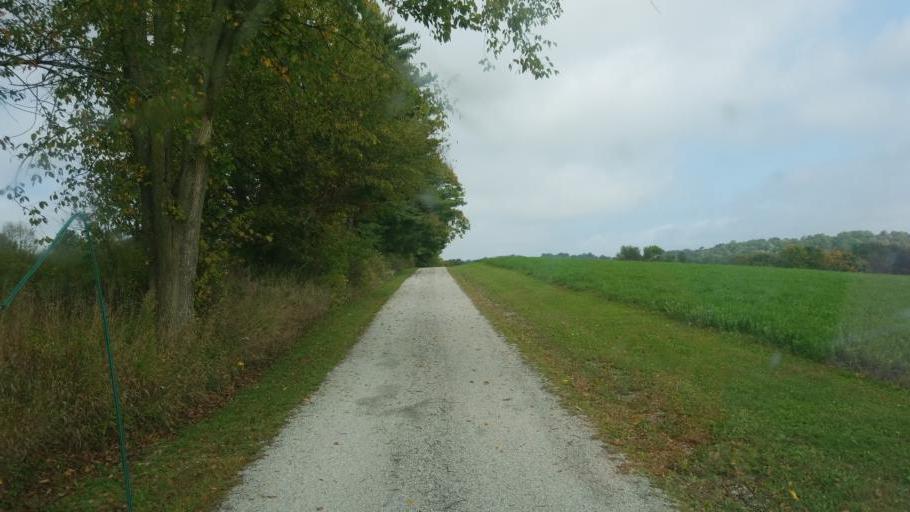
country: US
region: Ohio
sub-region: Richland County
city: Lincoln Heights
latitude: 40.7296
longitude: -82.4044
